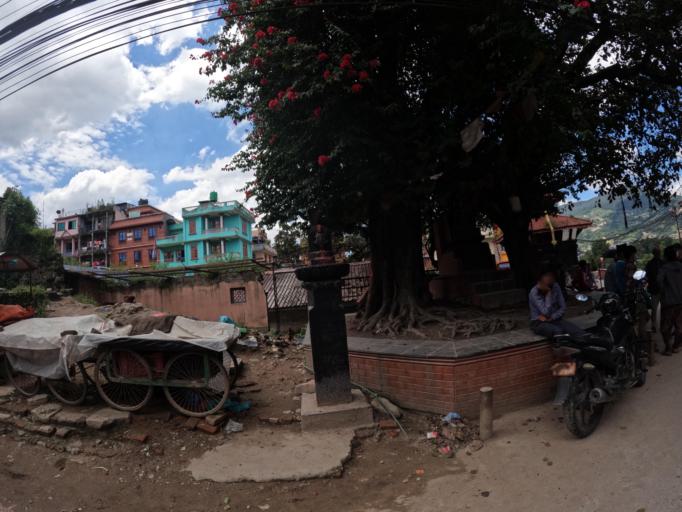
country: NP
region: Central Region
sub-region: Bagmati Zone
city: Kathmandu
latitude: 27.7686
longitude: 85.3303
